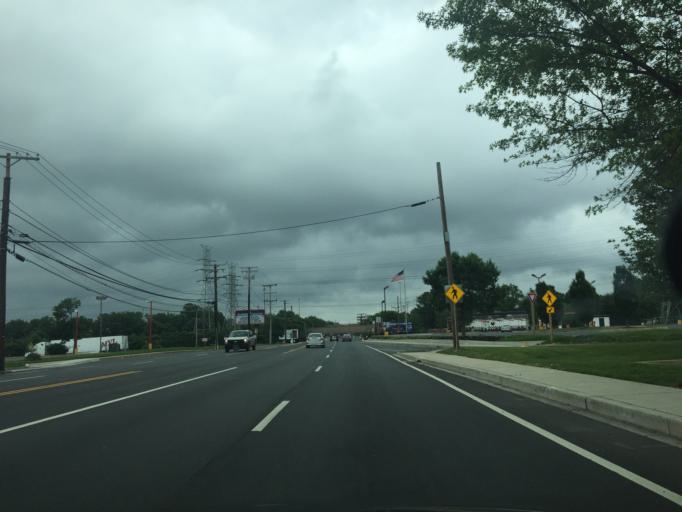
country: US
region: Maryland
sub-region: Baltimore County
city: Rosedale
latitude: 39.2959
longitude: -76.5081
